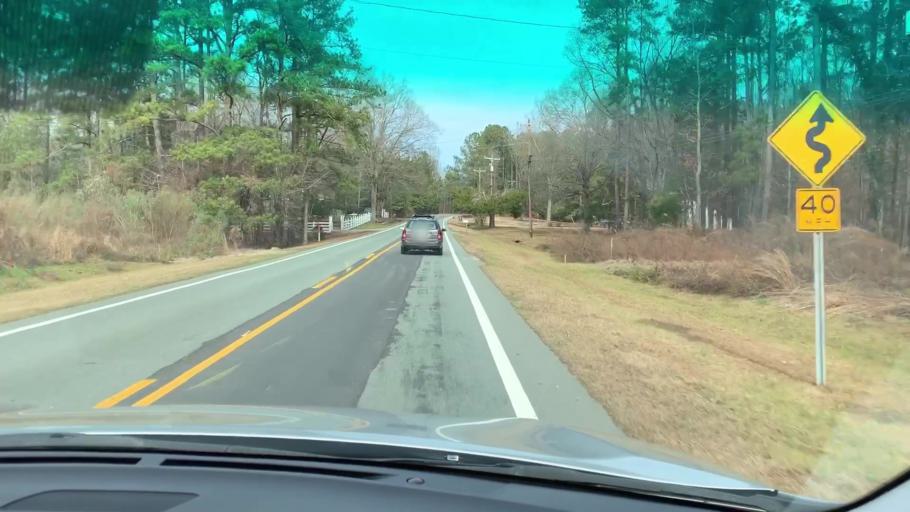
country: US
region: North Carolina
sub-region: Wake County
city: Green Level
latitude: 35.8581
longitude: -78.9407
